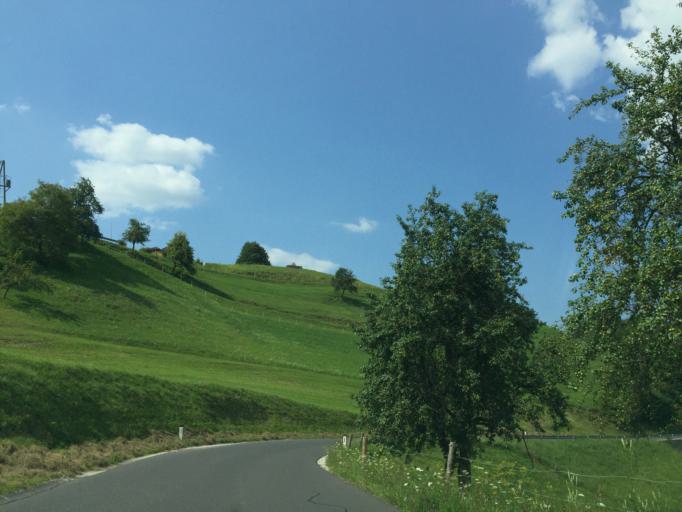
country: SI
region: Sostanj
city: Ravne
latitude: 46.4275
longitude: 15.1184
